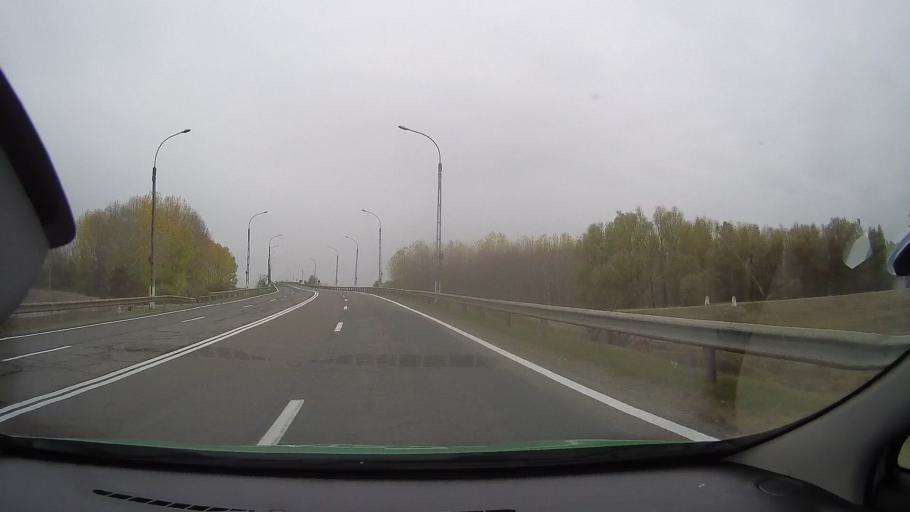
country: RO
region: Ialomita
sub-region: Comuna Giurgeni
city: Giurgeni
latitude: 44.7521
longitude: 27.8897
